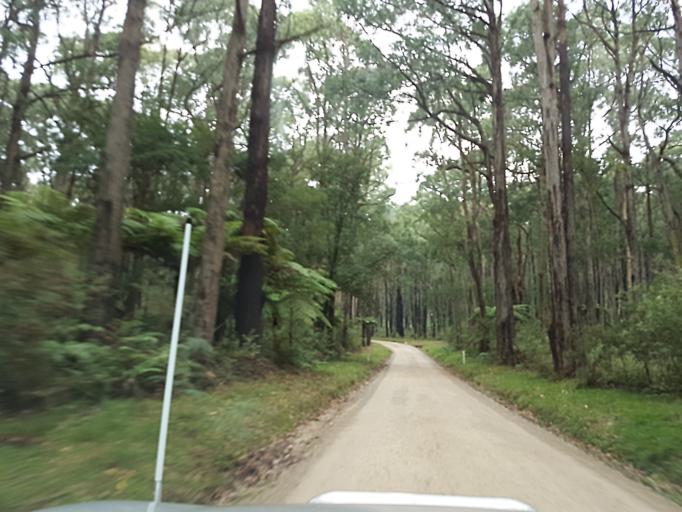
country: AU
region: Victoria
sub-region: Yarra Ranges
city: Olinda
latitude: -37.8426
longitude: 145.3969
